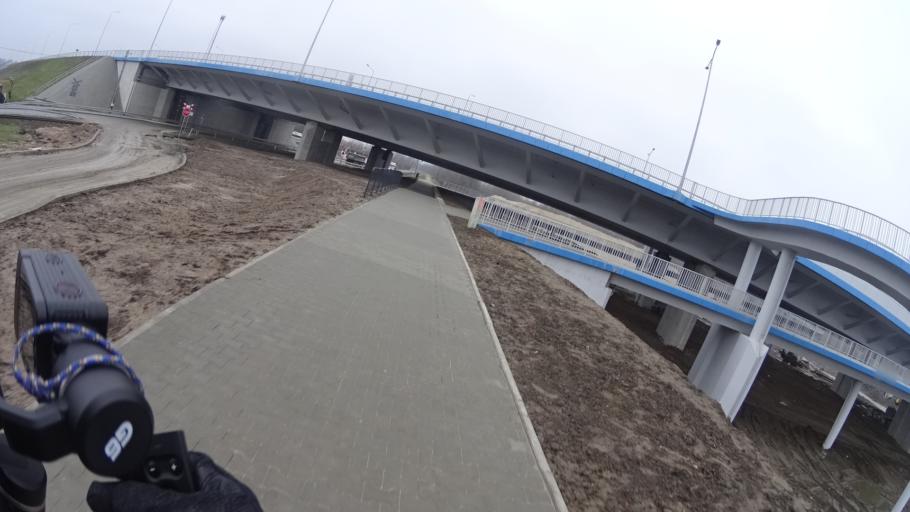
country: PL
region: Masovian Voivodeship
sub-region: Warszawa
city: Wilanow
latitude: 52.1596
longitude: 21.1368
